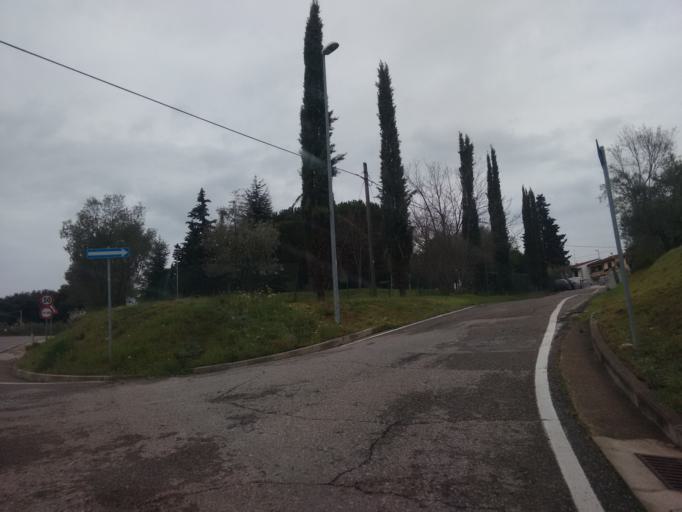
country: IT
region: Tuscany
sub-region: Province of Florence
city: Strada in Chianti
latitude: 43.6569
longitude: 11.2965
